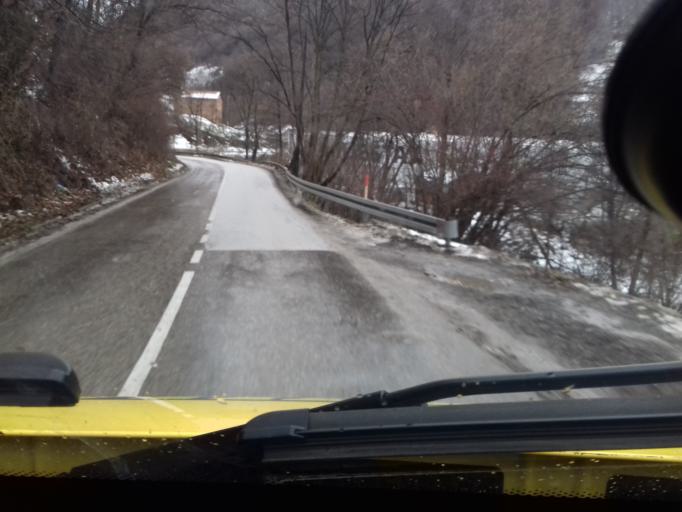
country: BA
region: Federation of Bosnia and Herzegovina
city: Lokvine
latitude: 44.1955
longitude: 17.8746
